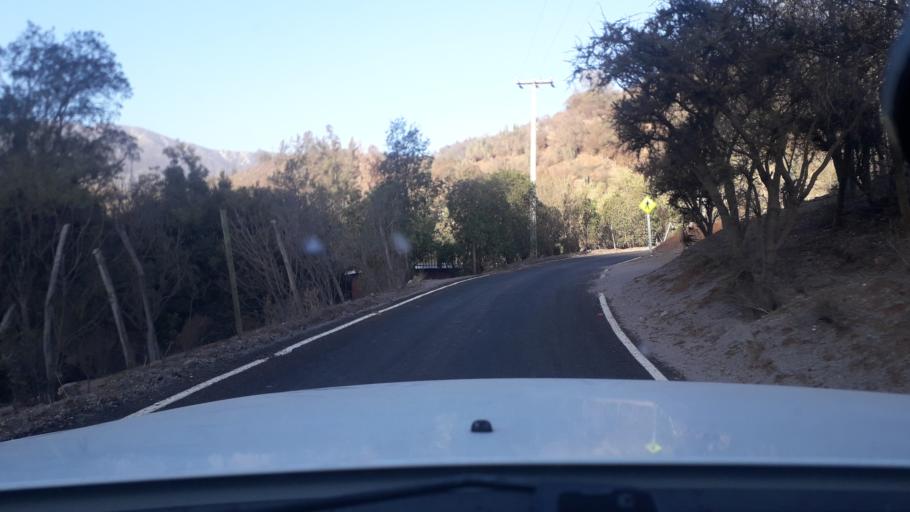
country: CL
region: Valparaiso
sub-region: Provincia de Marga Marga
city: Limache
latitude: -33.0461
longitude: -71.0596
